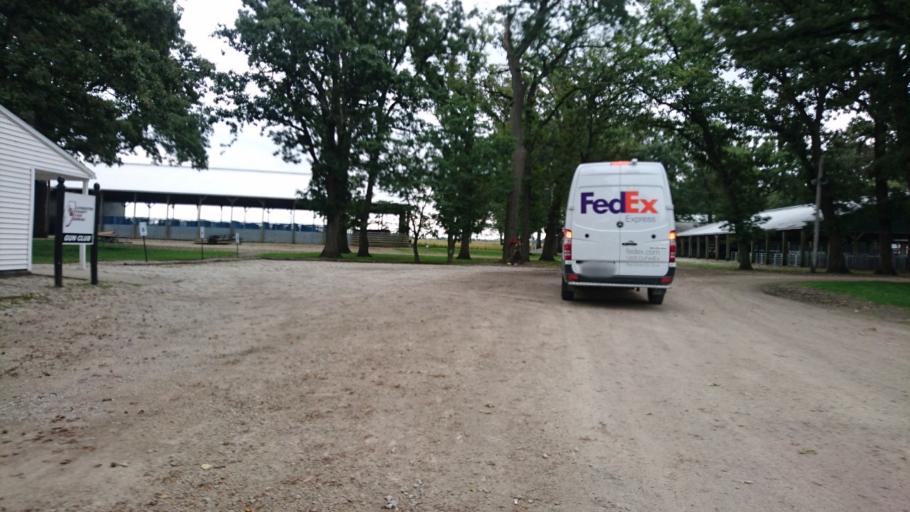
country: US
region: Illinois
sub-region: Livingston County
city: Pontiac
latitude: 40.8929
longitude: -88.6655
